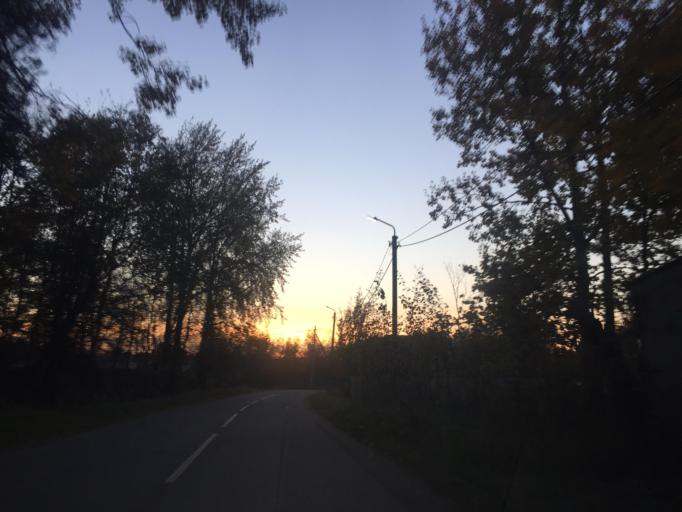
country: RU
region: Leningrad
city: Priozersk
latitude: 61.0333
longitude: 30.1339
